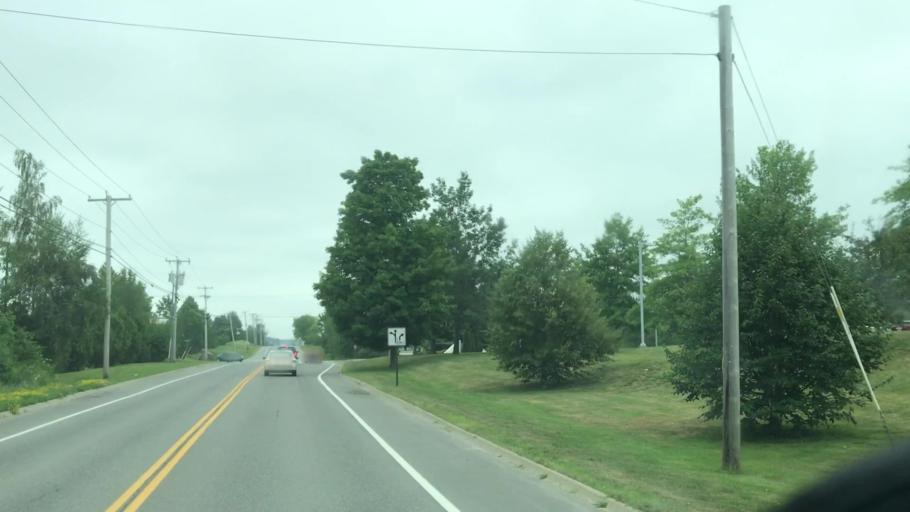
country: US
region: Maine
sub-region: Penobscot County
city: Veazie
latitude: 44.8459
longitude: -68.7402
